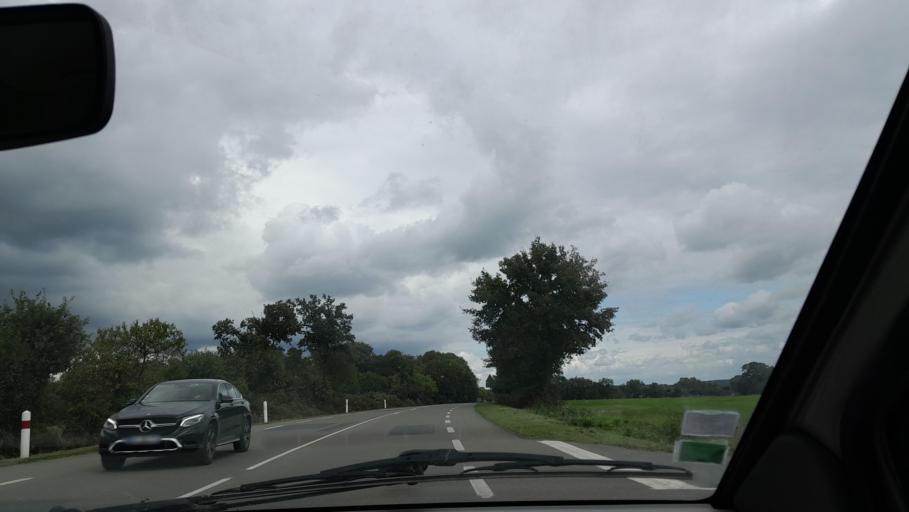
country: FR
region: Pays de la Loire
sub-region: Departement de la Mayenne
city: Ahuille
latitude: 47.9978
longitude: -0.8470
